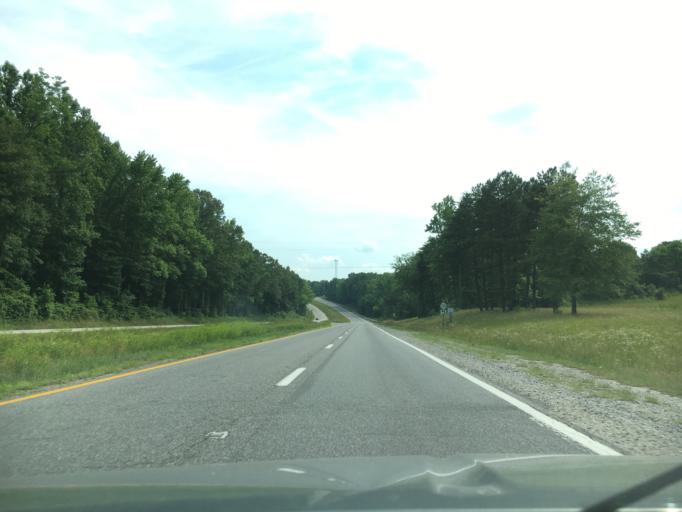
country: US
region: Virginia
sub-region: Prince Edward County
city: Hampden Sydney
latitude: 37.1015
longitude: -78.3736
